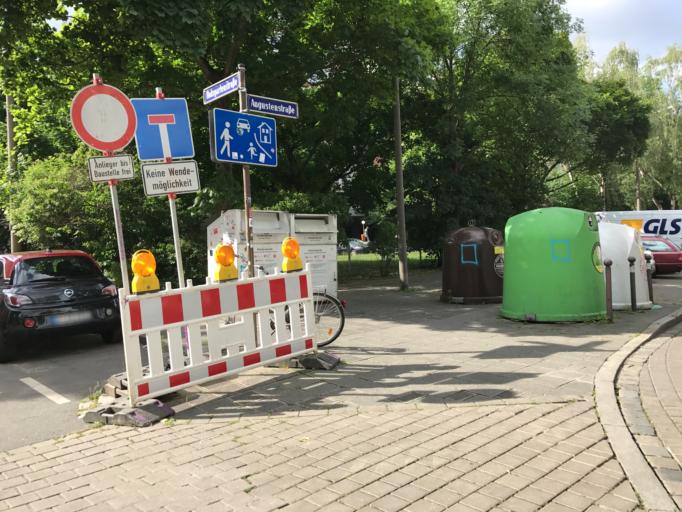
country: DE
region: Bavaria
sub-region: Regierungsbezirk Mittelfranken
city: Nuernberg
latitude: 49.4415
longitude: 11.0949
